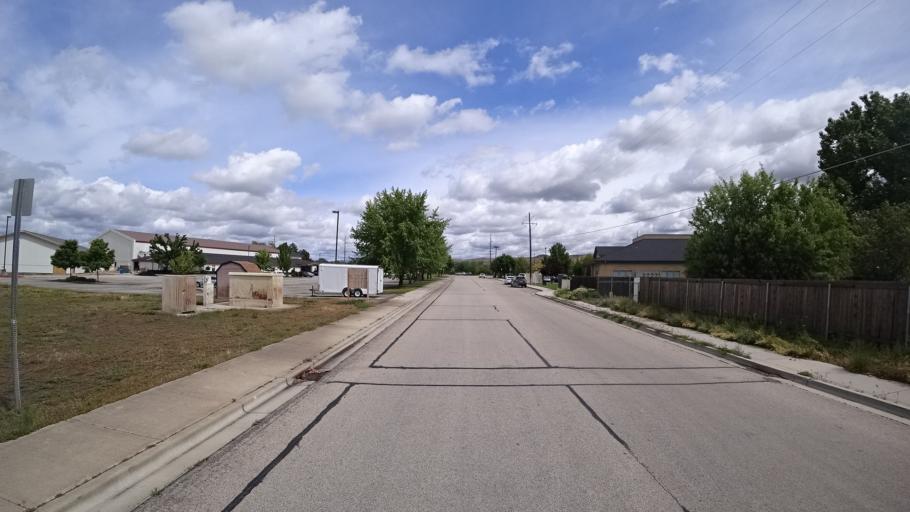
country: US
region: Idaho
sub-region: Ada County
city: Eagle
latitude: 43.6778
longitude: -116.3041
